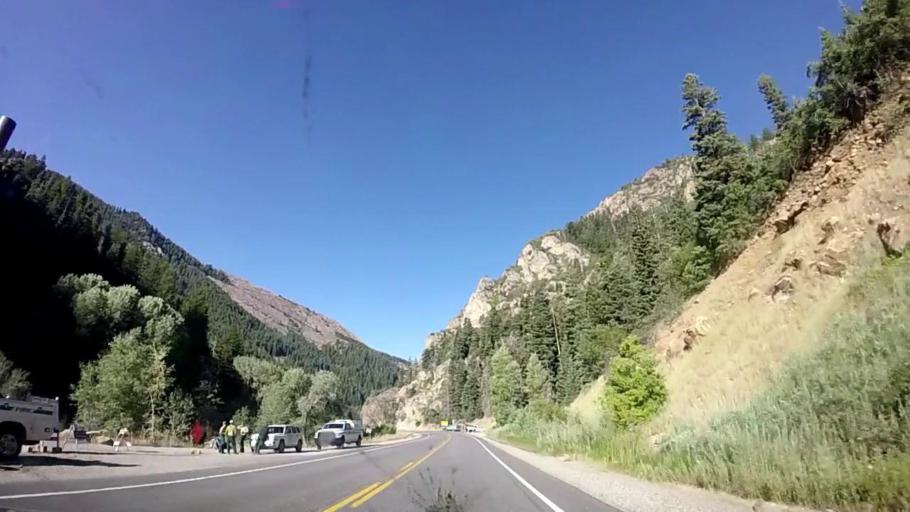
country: US
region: Utah
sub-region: Salt Lake County
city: Mount Olympus
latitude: 40.6368
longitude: -111.6982
